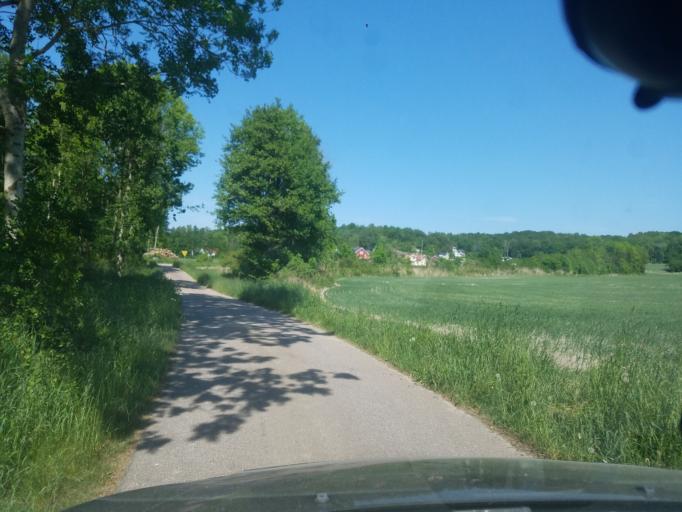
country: SE
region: Vaestra Goetaland
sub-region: Orust
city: Henan
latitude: 58.2652
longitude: 11.5712
